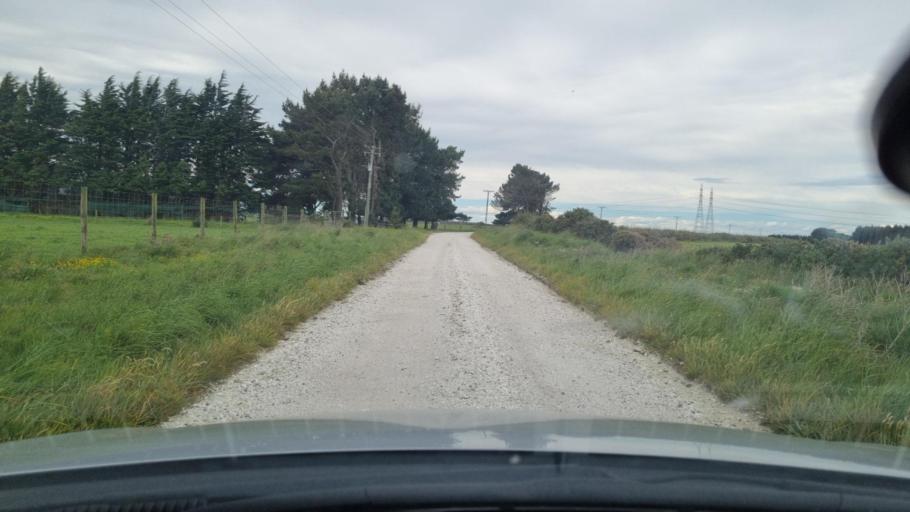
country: NZ
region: Southland
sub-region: Invercargill City
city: Invercargill
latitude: -46.4926
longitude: 168.4270
